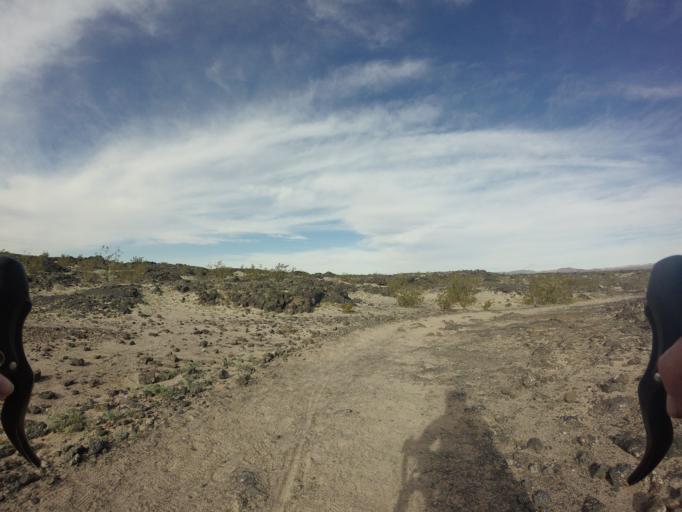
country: US
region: California
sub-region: San Bernardino County
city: Twentynine Palms
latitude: 34.5518
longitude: -115.7849
